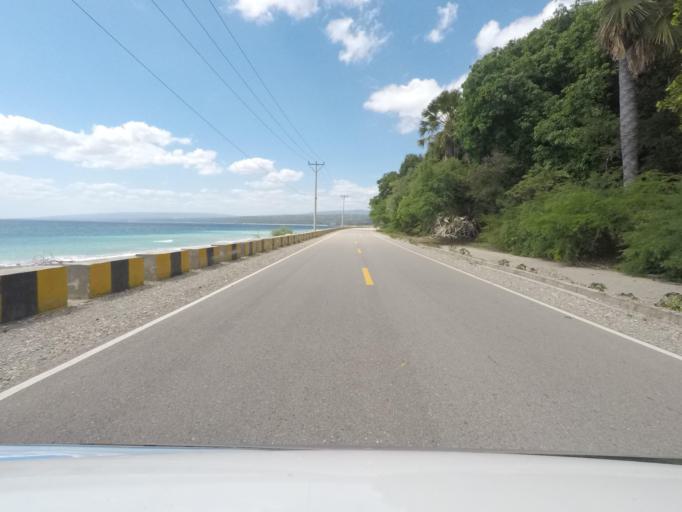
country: TL
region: Lautem
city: Lospalos
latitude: -8.4146
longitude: 126.7457
